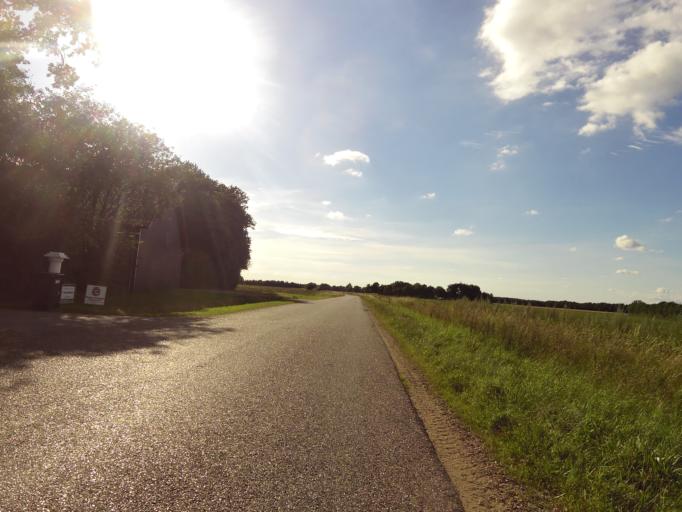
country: DK
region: South Denmark
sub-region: Haderslev Kommune
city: Vojens
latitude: 55.2053
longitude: 9.2745
